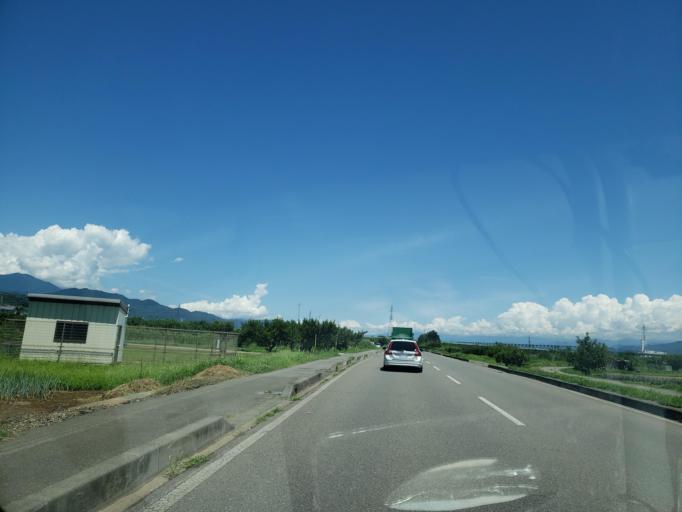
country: JP
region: Nagano
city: Nagano-shi
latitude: 36.5476
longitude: 138.1165
